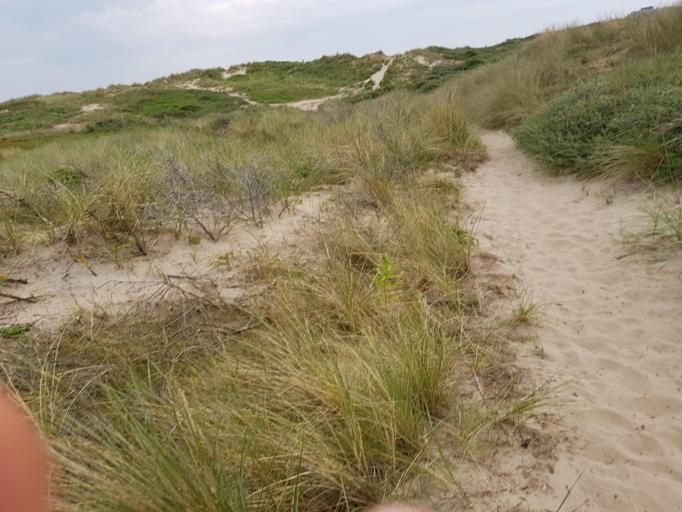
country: NL
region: North Holland
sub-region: Gemeente Bergen
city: Egmond aan Zee
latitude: 52.6273
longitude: 4.6248
